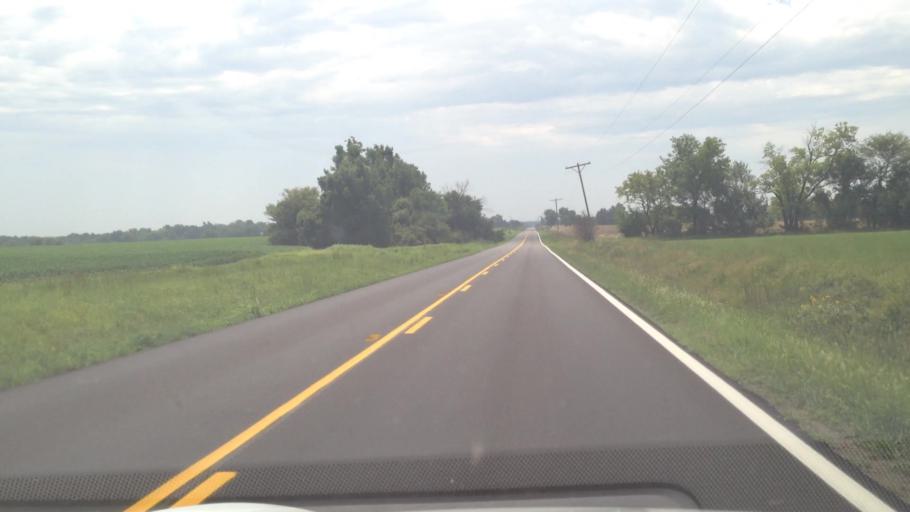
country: US
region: Kansas
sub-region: Crawford County
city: Girard
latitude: 37.6358
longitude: -94.9698
